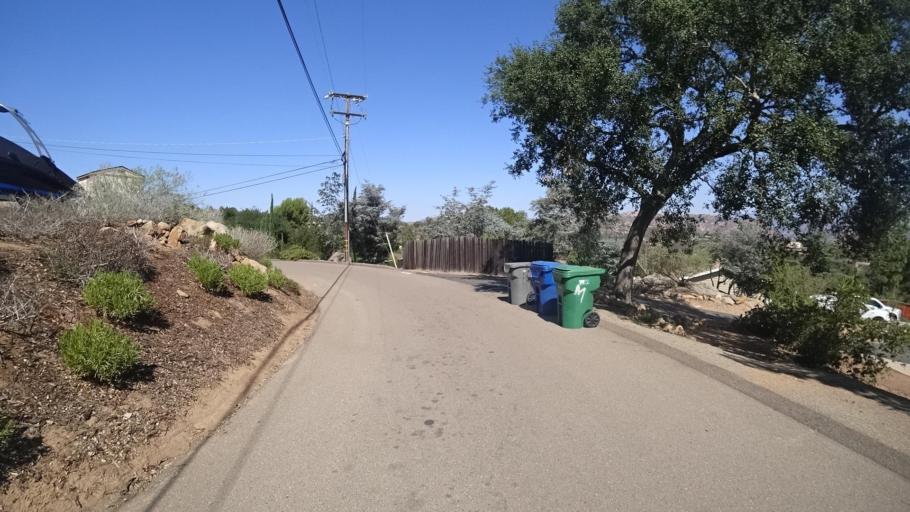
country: US
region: California
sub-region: San Diego County
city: Crest
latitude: 32.8091
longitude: -116.8599
